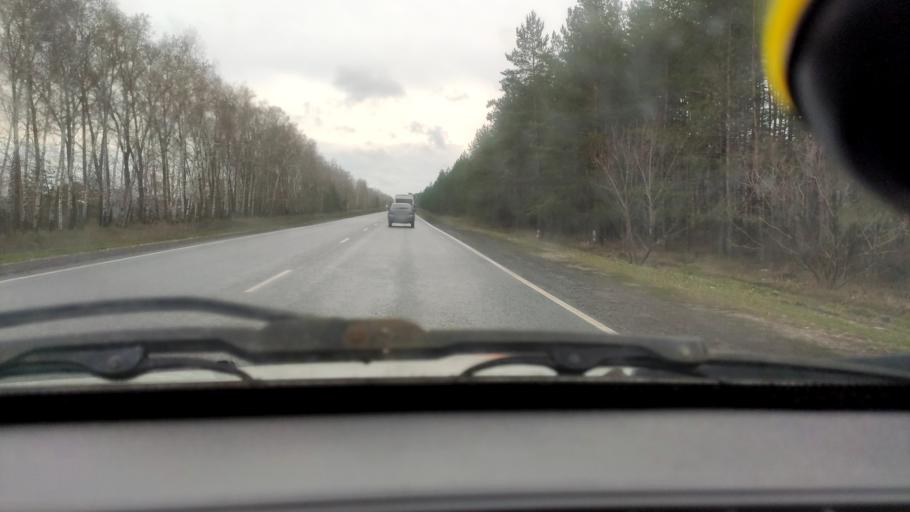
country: RU
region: Samara
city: Povolzhskiy
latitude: 53.6139
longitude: 49.6251
